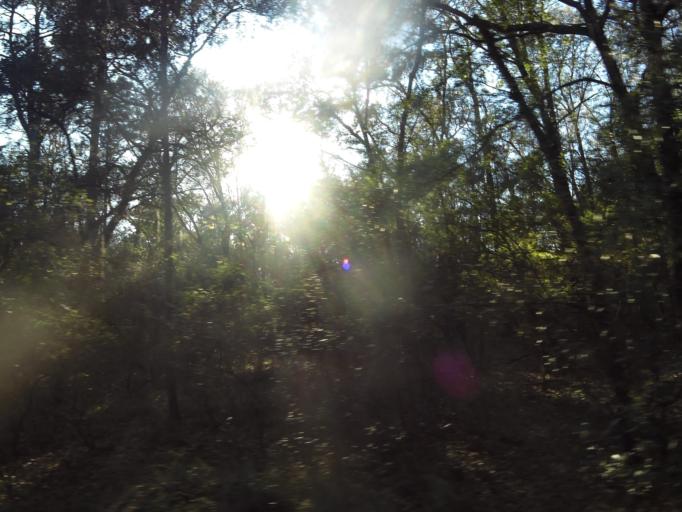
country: US
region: Florida
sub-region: Clay County
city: Middleburg
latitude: 30.1429
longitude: -81.9067
